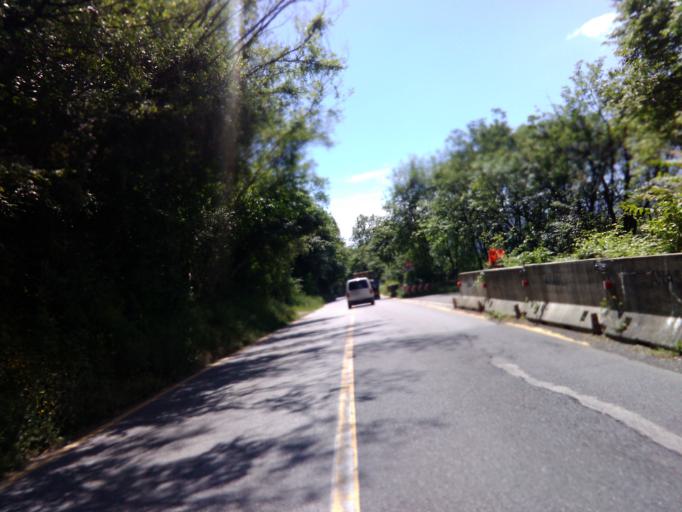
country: IT
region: Tuscany
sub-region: Provincia di Massa-Carrara
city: Barbarasco
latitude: 44.2627
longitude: 9.9542
